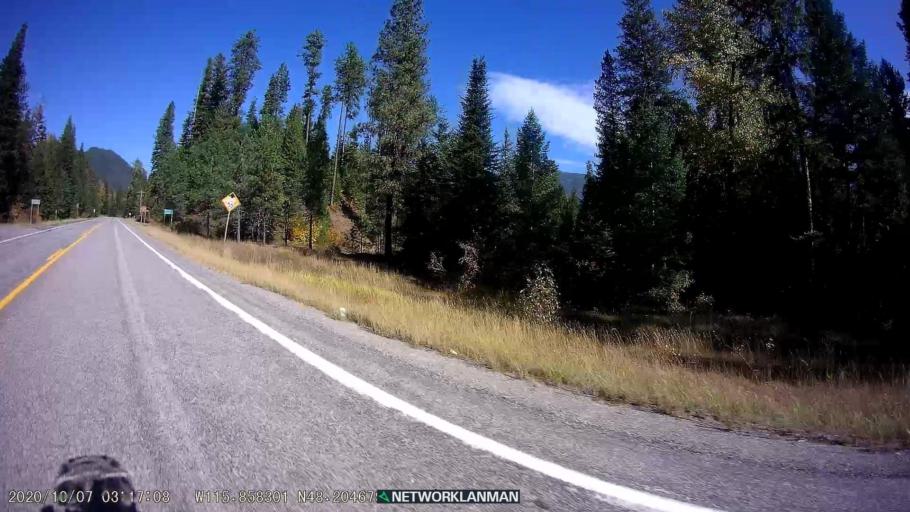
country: US
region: Montana
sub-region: Lincoln County
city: Libby
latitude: 48.2051
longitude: -115.8583
